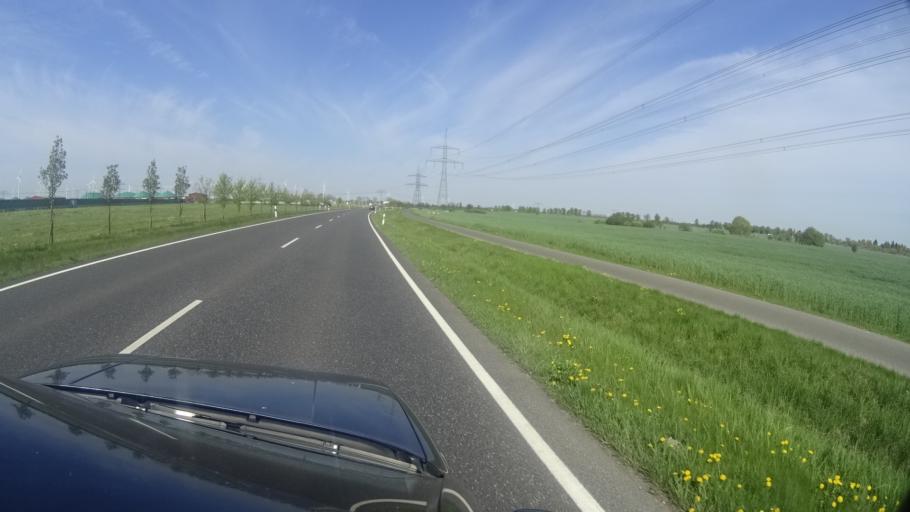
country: DE
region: Brandenburg
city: Nauen
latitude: 52.5946
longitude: 12.8630
